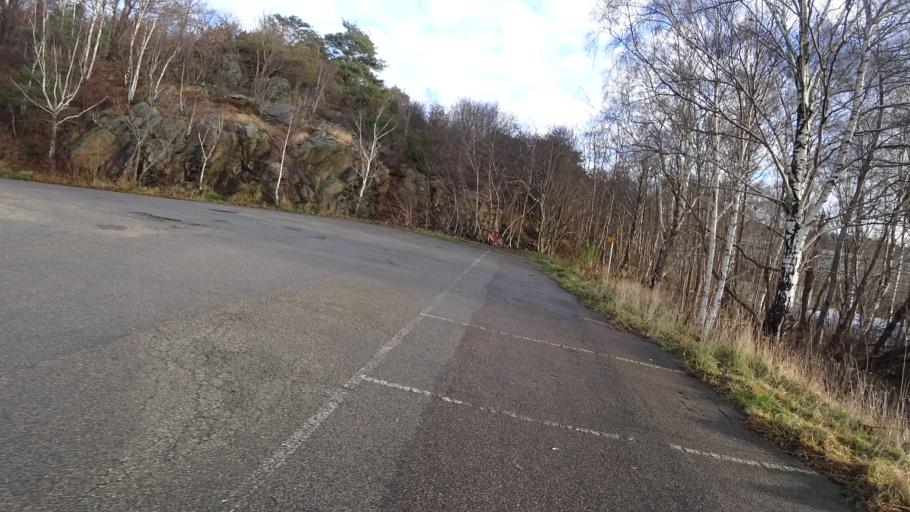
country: SE
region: Vaestra Goetaland
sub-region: Goteborg
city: Majorna
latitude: 57.6666
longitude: 11.9409
